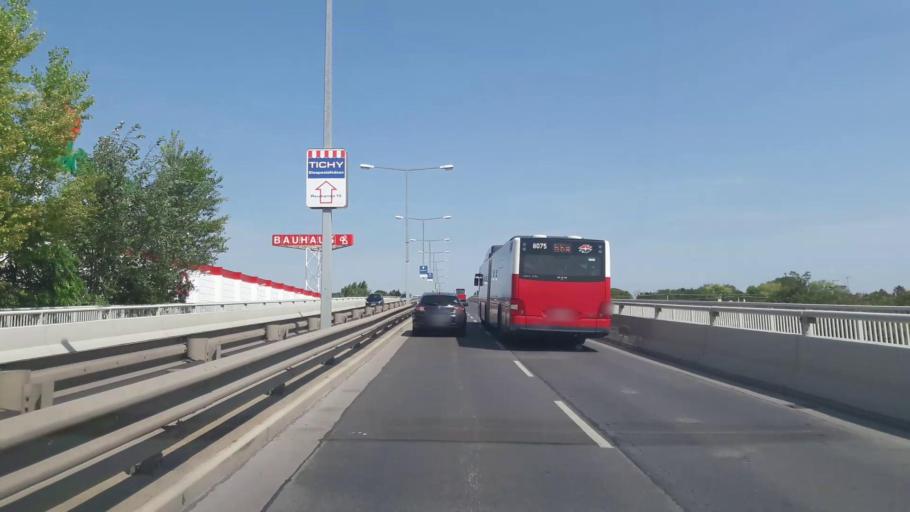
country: AT
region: Lower Austria
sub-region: Politischer Bezirk Modling
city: Vosendorf
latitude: 48.1493
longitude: 16.3620
